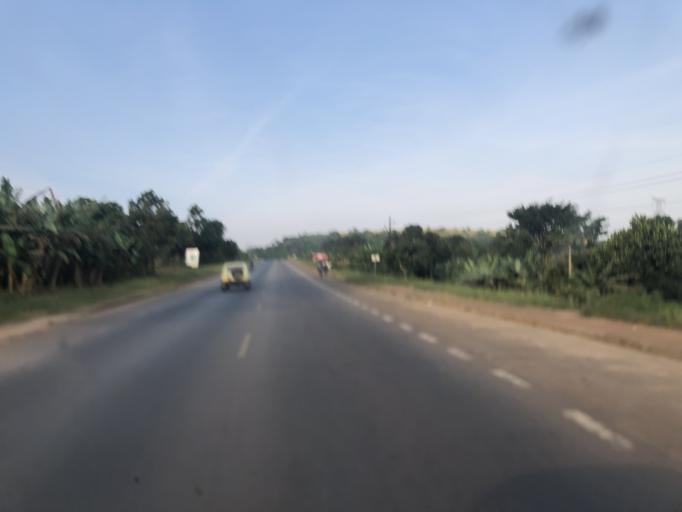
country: UG
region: Central Region
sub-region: Mpigi District
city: Mpigi
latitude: 0.1728
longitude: 32.2689
